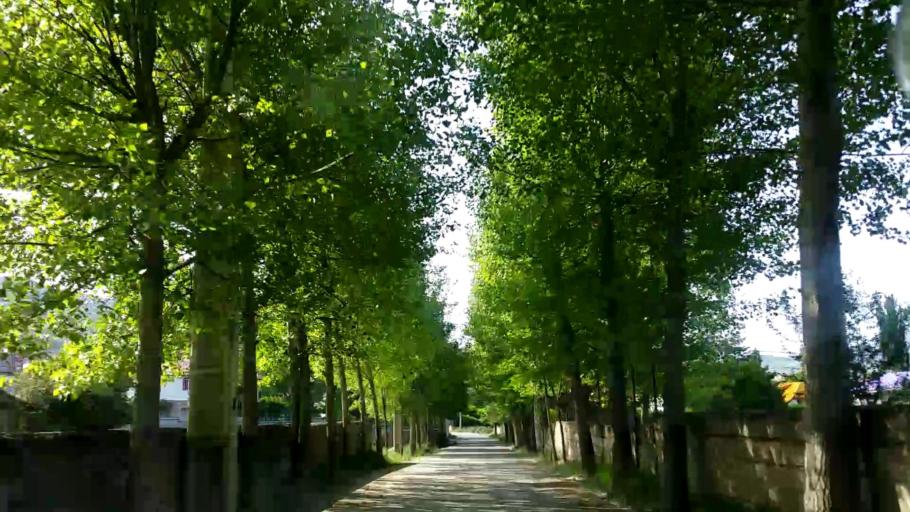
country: IR
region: Mazandaran
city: `Abbasabad
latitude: 36.5202
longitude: 51.1737
